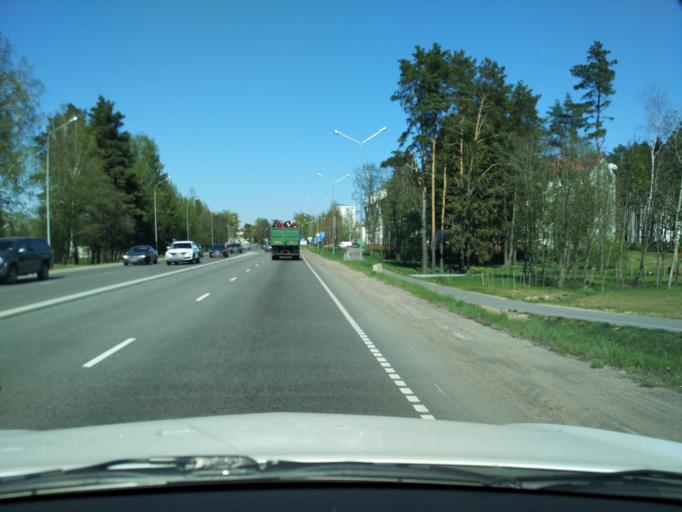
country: BY
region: Minsk
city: Borovlyany
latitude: 53.9903
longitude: 27.6675
